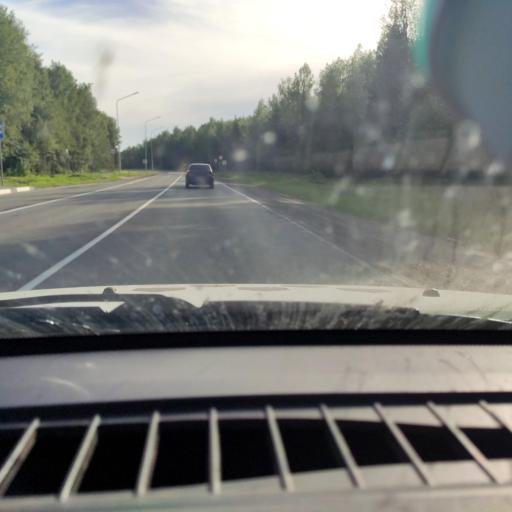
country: RU
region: Kirov
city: Vakhrushi
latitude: 58.6661
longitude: 49.9304
